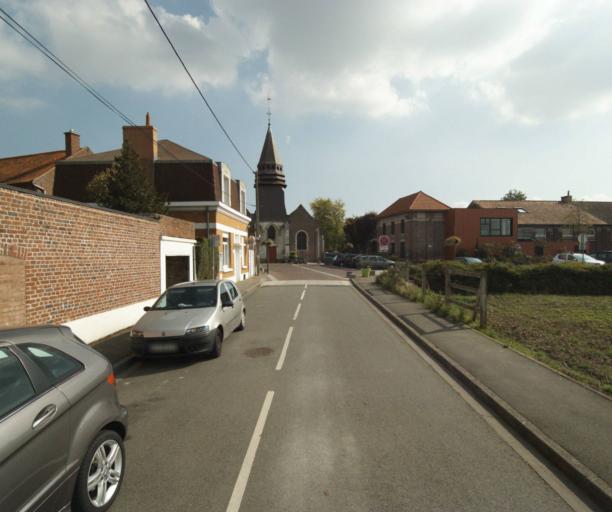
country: FR
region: Nord-Pas-de-Calais
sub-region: Departement du Nord
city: Houplin-Ancoisne
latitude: 50.5620
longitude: 3.0000
